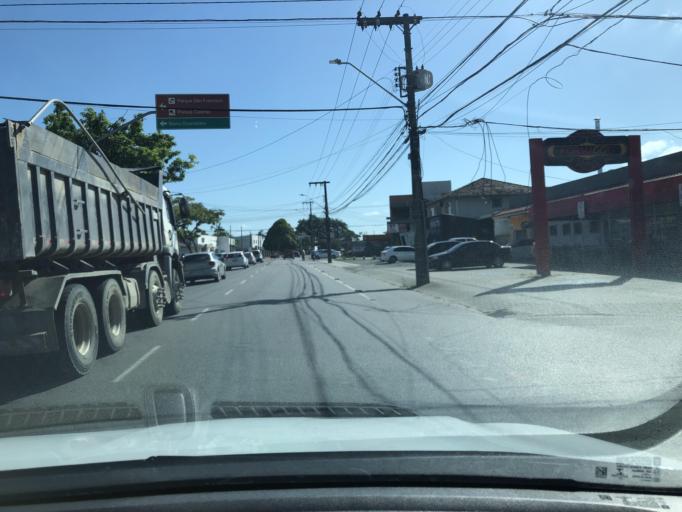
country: BR
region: Santa Catarina
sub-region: Joinville
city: Joinville
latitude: -26.3205
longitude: -48.8319
